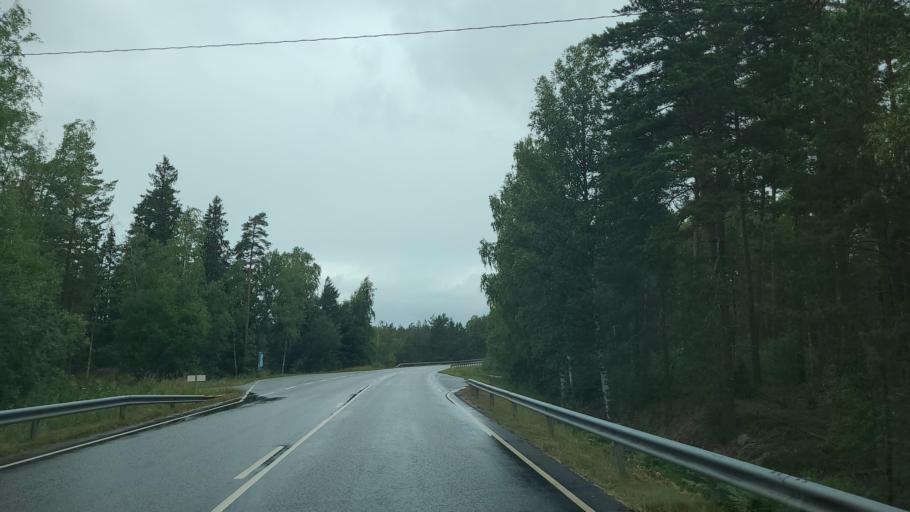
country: FI
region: Varsinais-Suomi
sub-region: Aboland-Turunmaa
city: Kimito
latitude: 60.2315
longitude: 22.6073
